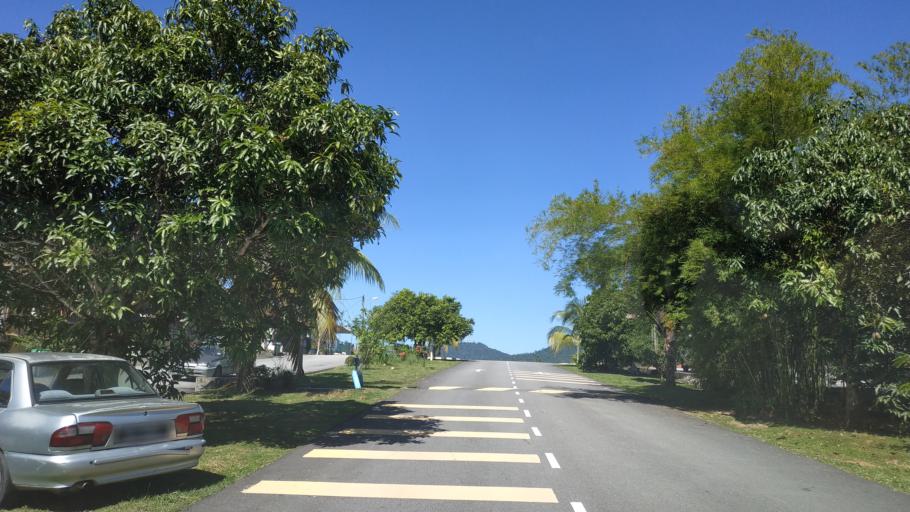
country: MY
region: Kedah
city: Kulim
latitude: 5.3384
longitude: 100.5354
